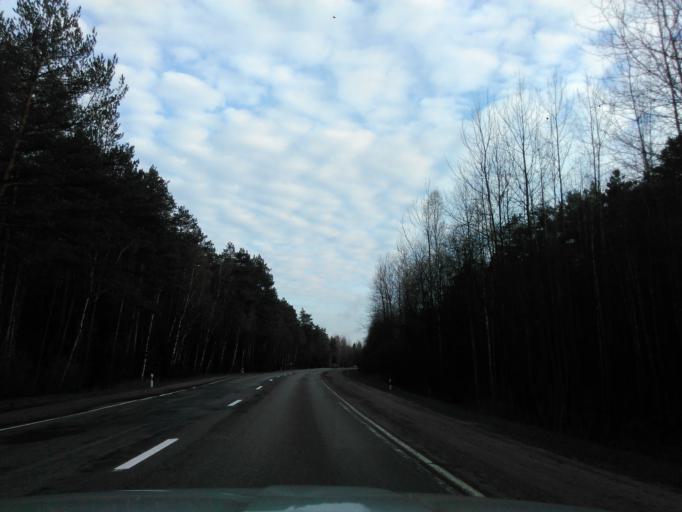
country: BY
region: Minsk
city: Plyeshchanitsy
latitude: 54.3742
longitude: 27.8817
